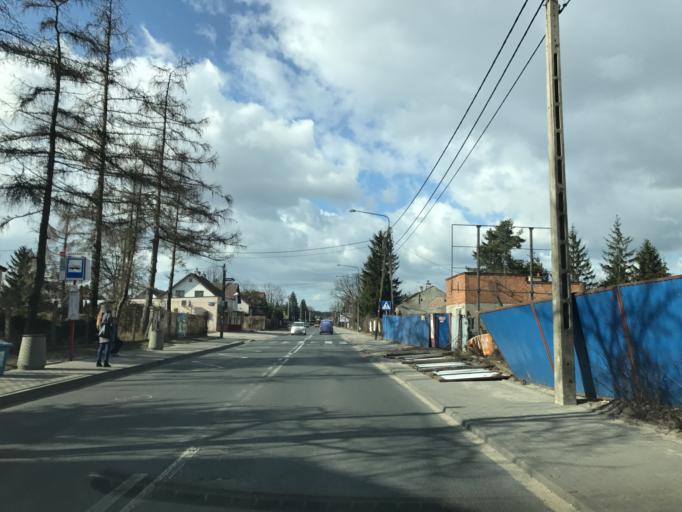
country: PL
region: Masovian Voivodeship
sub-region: Warszawa
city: Rembertow
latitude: 52.2677
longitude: 21.1533
